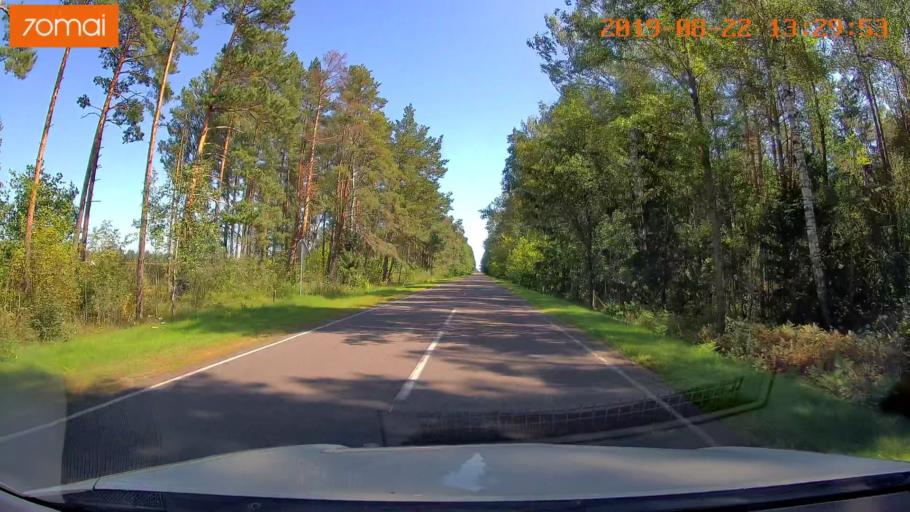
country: BY
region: Minsk
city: Staryya Darohi
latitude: 53.2173
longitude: 28.1426
